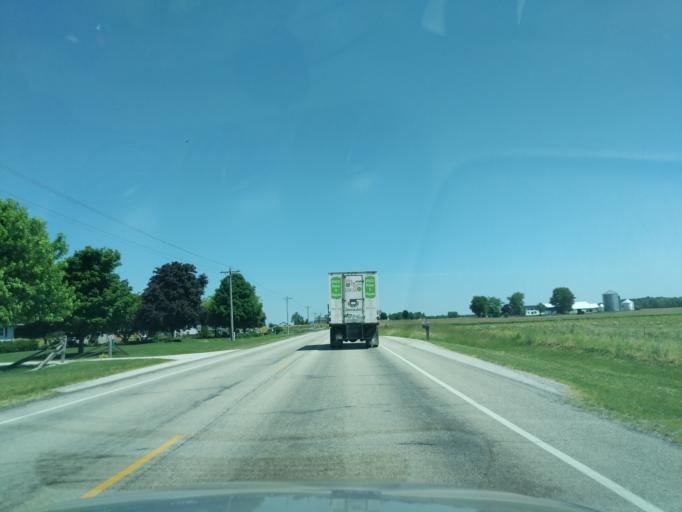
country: US
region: Indiana
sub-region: Huntington County
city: Roanoke
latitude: 41.0134
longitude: -85.4707
